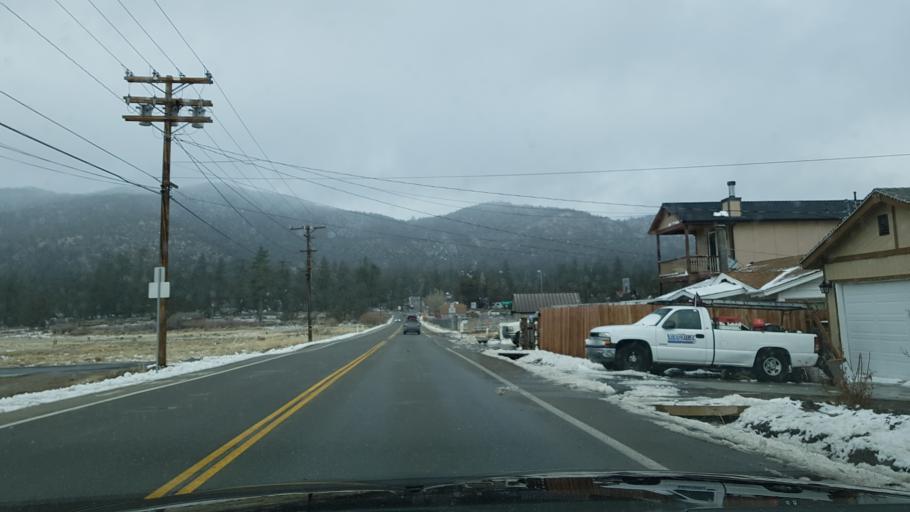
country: US
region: California
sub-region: San Bernardino County
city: Big Bear City
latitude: 34.2619
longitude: -116.8662
